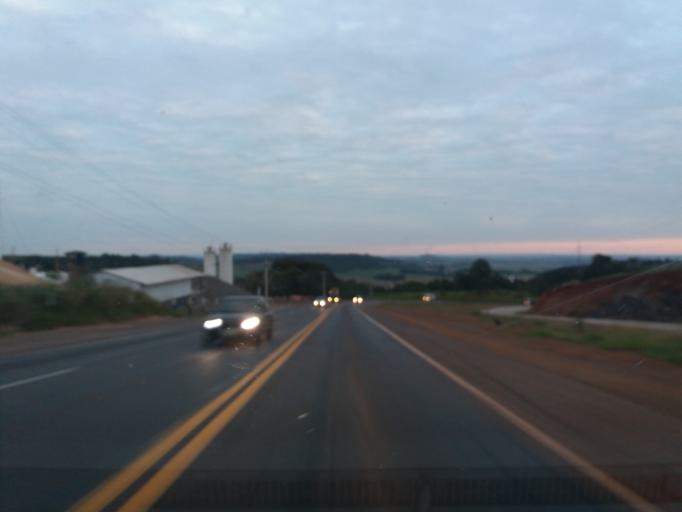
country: BR
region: Parana
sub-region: Realeza
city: Realeza
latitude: -25.3693
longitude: -53.5729
